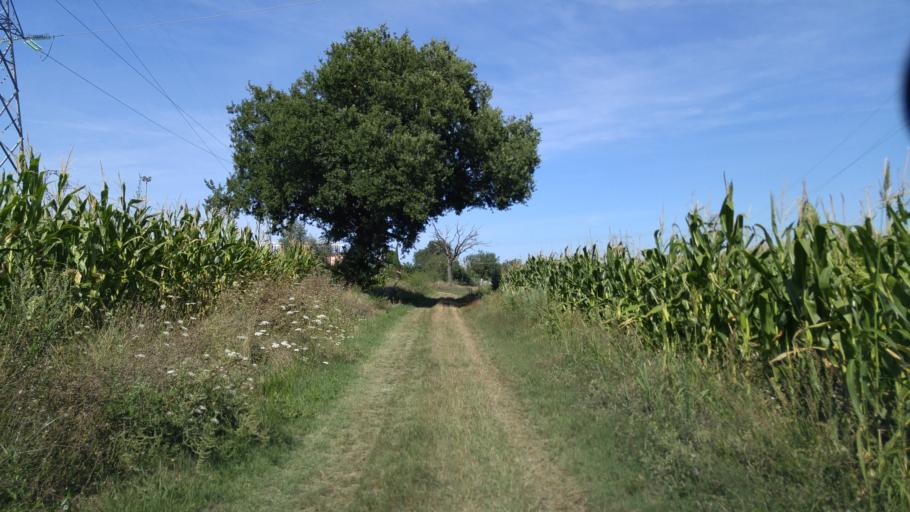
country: IT
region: The Marches
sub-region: Provincia di Pesaro e Urbino
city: Cuccurano
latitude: 43.7851
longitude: 12.9552
